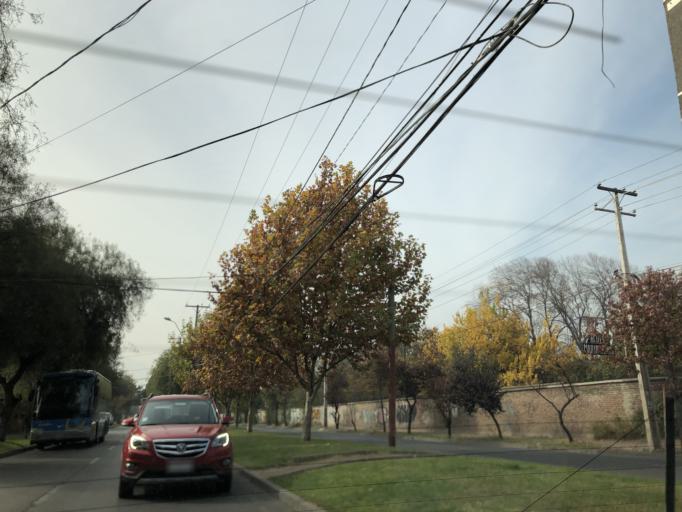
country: CL
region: Santiago Metropolitan
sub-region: Provincia de Cordillera
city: Puente Alto
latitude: -33.5802
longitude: -70.5755
